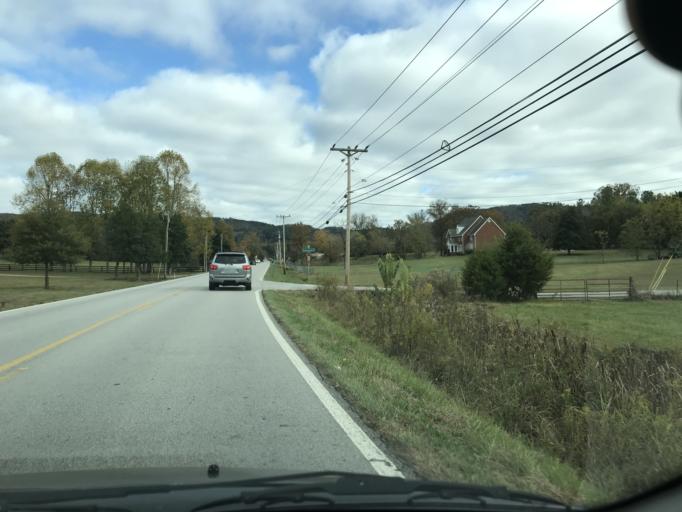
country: US
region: Tennessee
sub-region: Hamilton County
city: Lakesite
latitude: 35.1773
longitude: -85.0343
